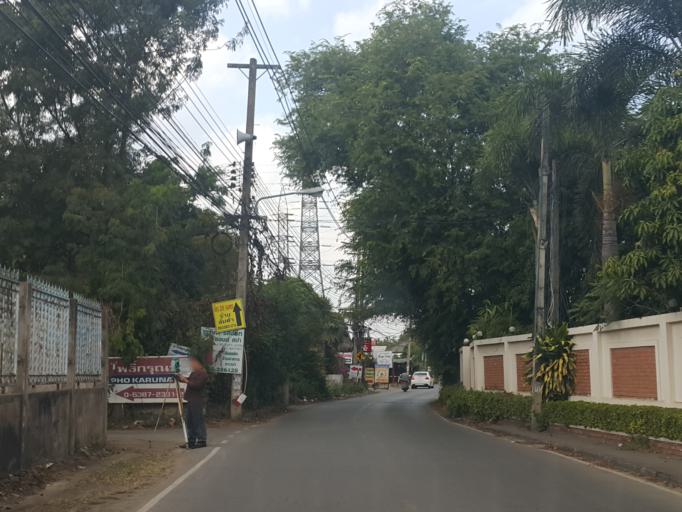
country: TH
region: Chiang Mai
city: Chiang Mai
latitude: 18.8136
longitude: 99.0013
